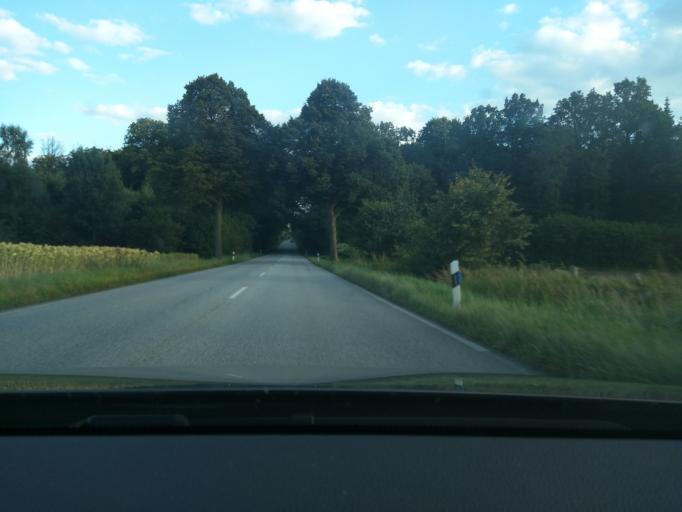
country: DE
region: Schleswig-Holstein
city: Grabau
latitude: 53.4819
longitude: 10.5278
